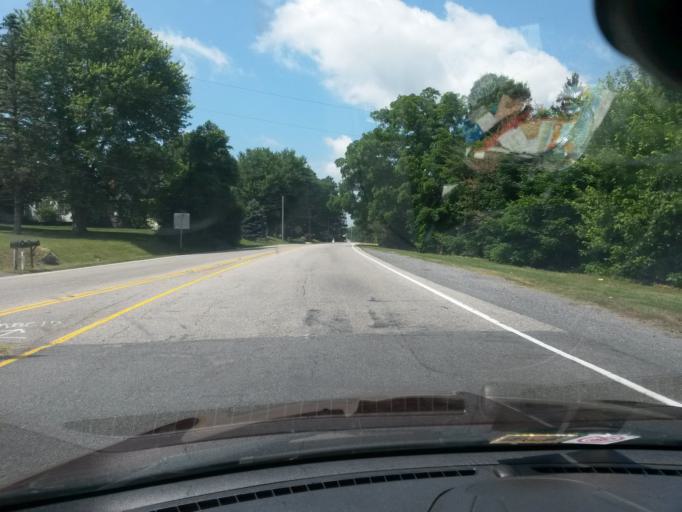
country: US
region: Virginia
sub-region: City of Buena Vista
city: Buena Vista
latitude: 37.8816
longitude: -79.2851
